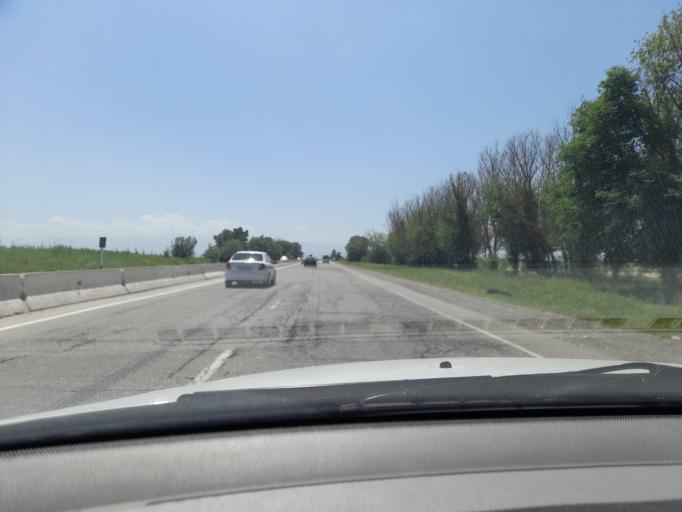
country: UZ
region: Jizzax
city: Jizzax
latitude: 40.1671
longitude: 67.9615
